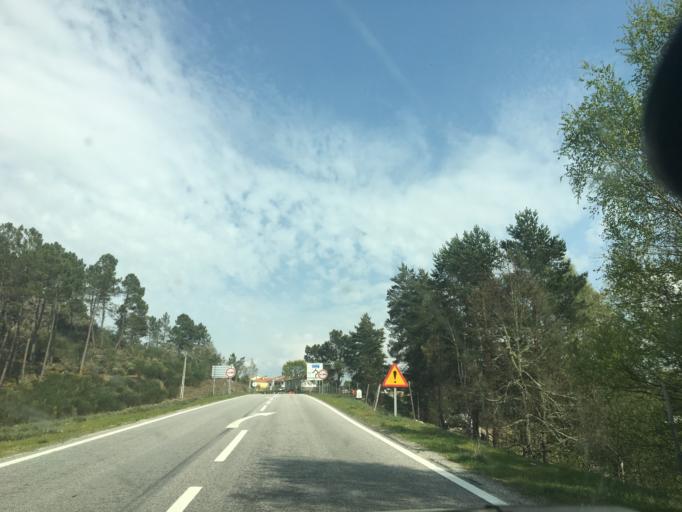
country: PT
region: Vila Real
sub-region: Boticas
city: Boticas
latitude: 41.6803
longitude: -7.7073
